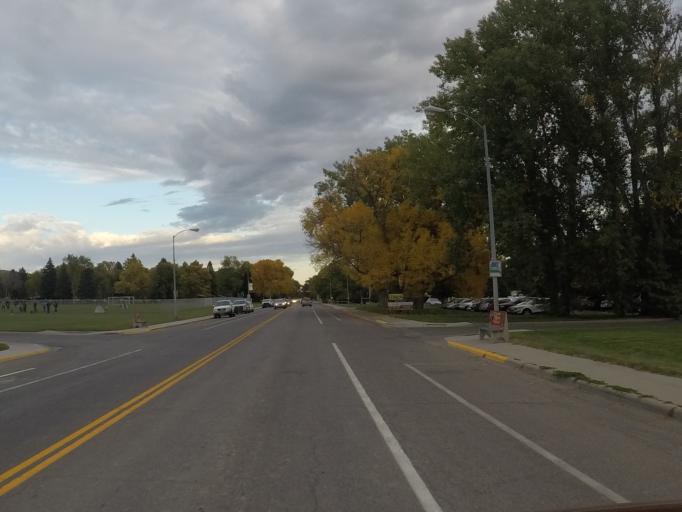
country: US
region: Montana
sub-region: Yellowstone County
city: Billings
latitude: 45.7949
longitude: -108.5535
